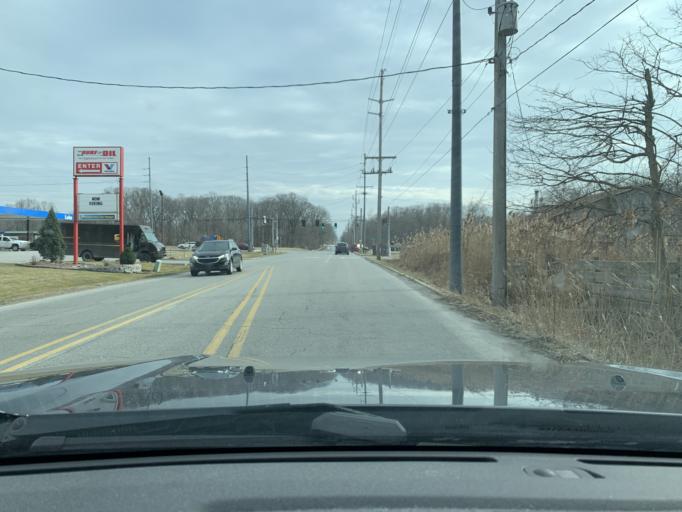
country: US
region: Indiana
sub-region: Porter County
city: Chesterton
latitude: 41.5509
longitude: -87.0664
